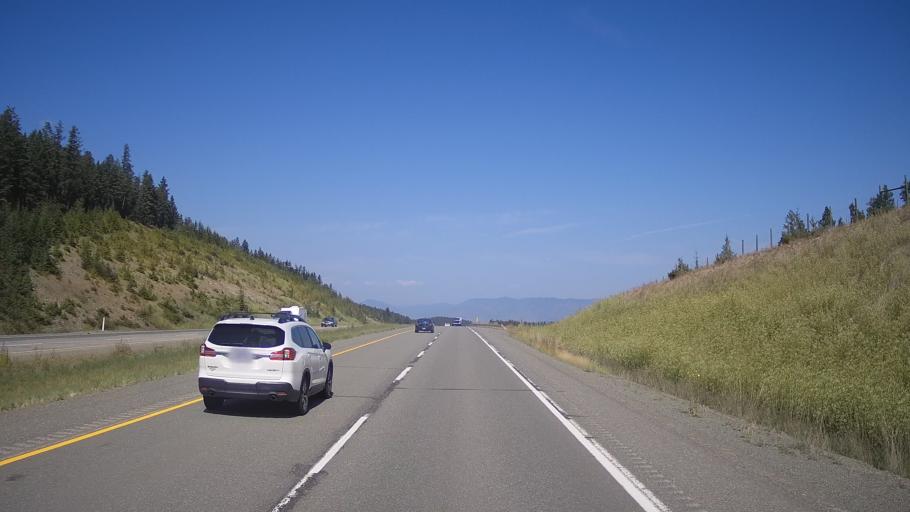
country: CA
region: British Columbia
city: Kamloops
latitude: 50.5827
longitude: -120.4677
